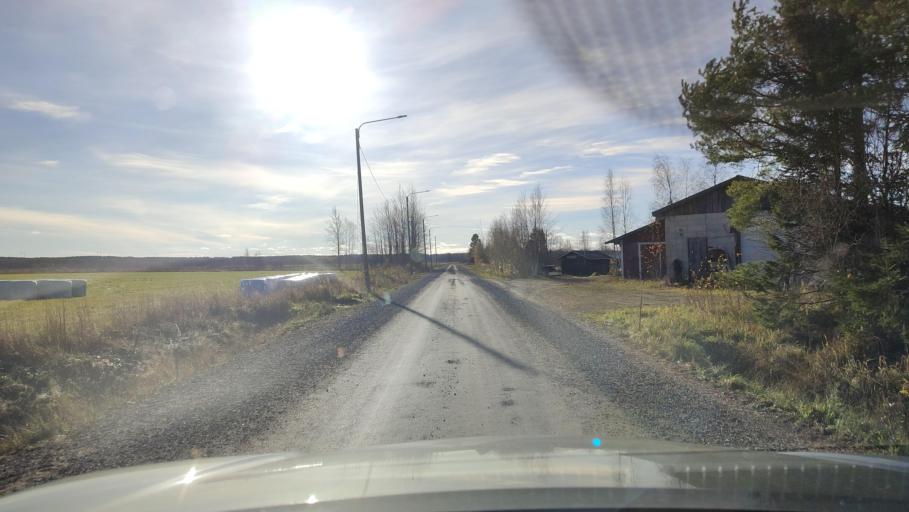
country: FI
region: Southern Ostrobothnia
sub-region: Suupohja
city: Teuva
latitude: 62.4485
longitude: 21.6132
